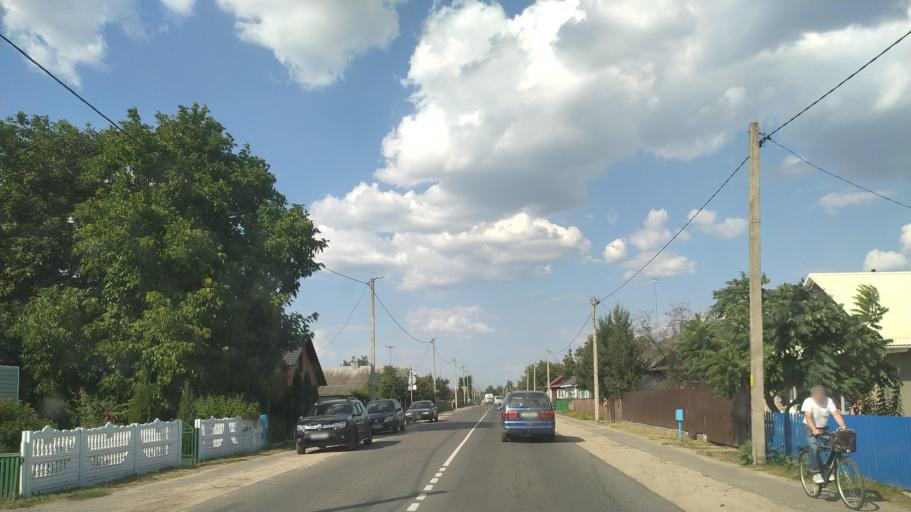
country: BY
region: Brest
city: Drahichyn
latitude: 52.1948
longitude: 25.1475
